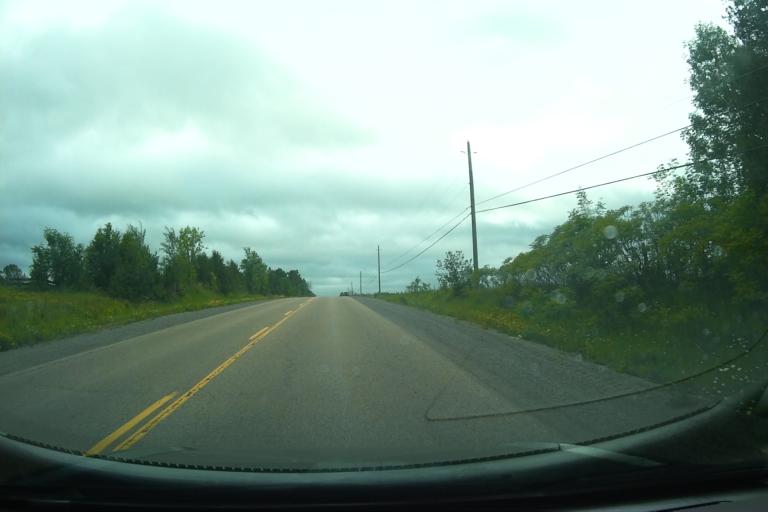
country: CA
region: Ontario
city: Pembroke
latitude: 45.5042
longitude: -77.1280
